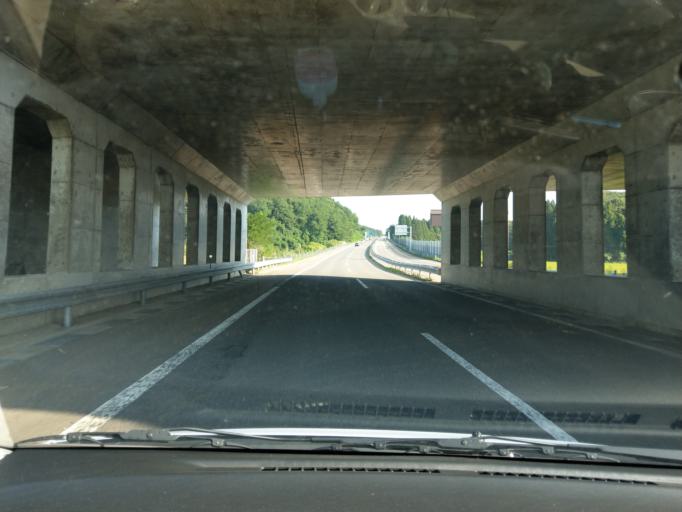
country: JP
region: Akita
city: Akita
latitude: 39.6371
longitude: 140.1911
